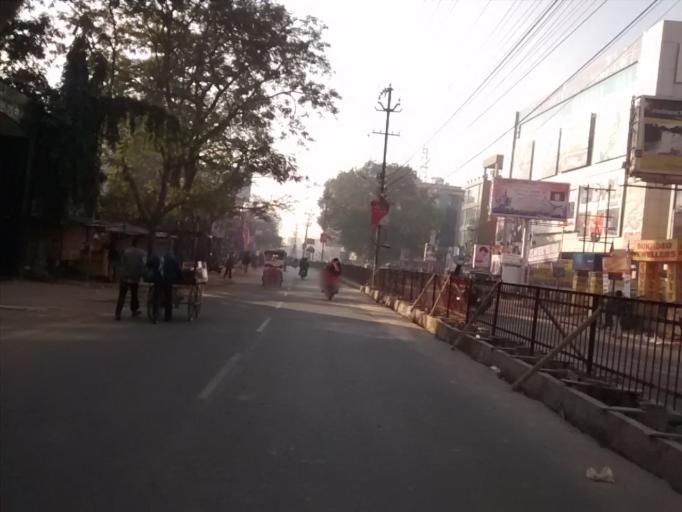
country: IN
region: Jharkhand
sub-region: Ranchi
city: Ranchi
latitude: 23.3524
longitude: 85.3249
